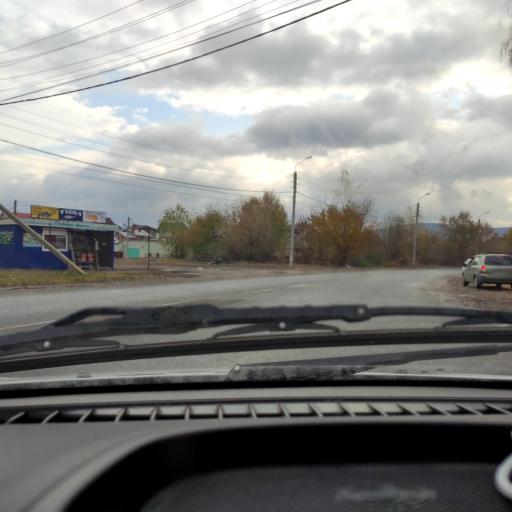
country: RU
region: Samara
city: Zhigulevsk
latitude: 53.4663
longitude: 49.6204
